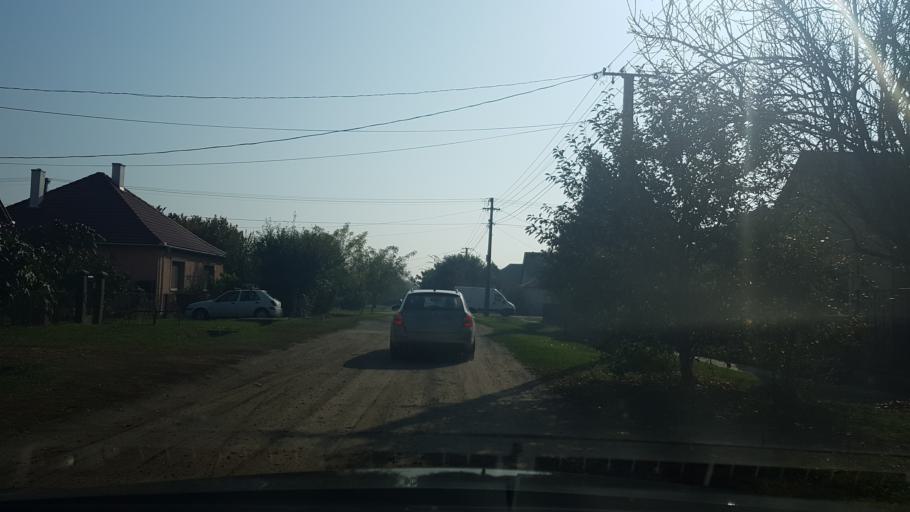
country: HU
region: Fejer
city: Pusztaszabolcs
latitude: 47.1457
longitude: 18.7582
